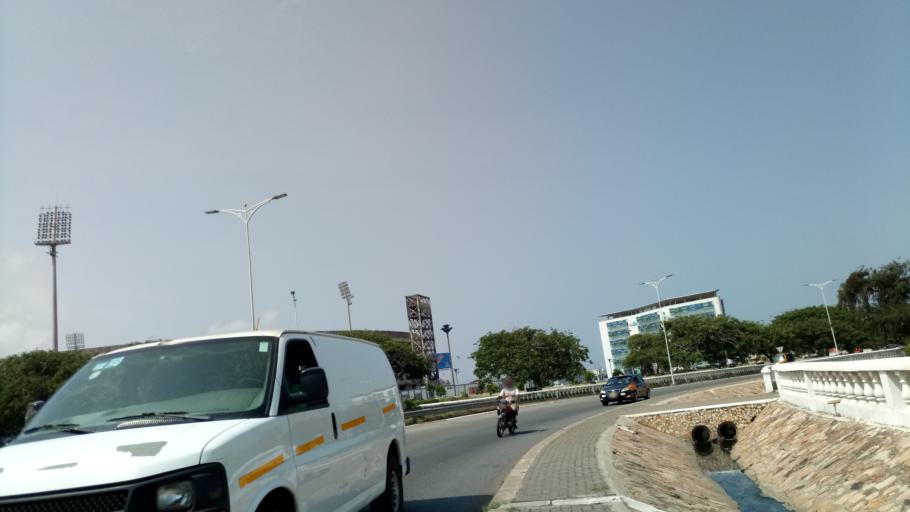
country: GH
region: Greater Accra
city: Accra
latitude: 5.5493
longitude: -0.1932
